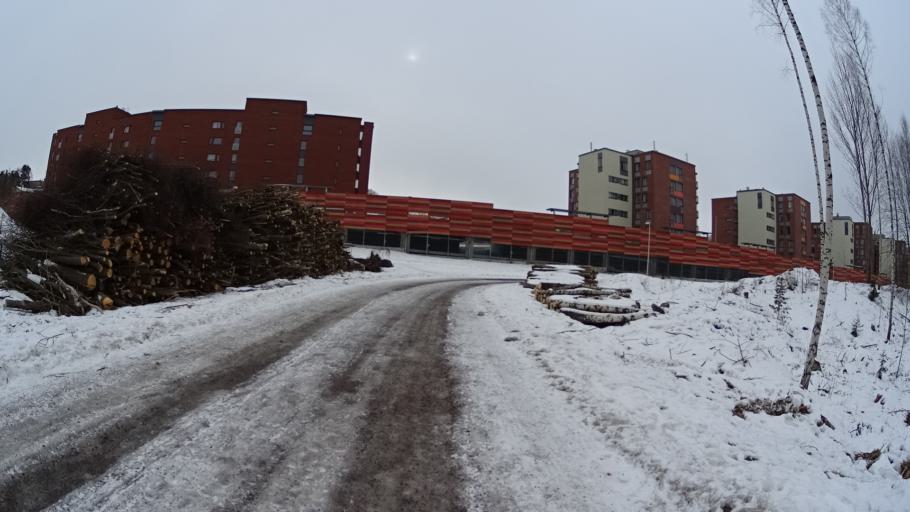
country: FI
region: Uusimaa
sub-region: Helsinki
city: Teekkarikylae
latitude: 60.2558
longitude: 24.8688
